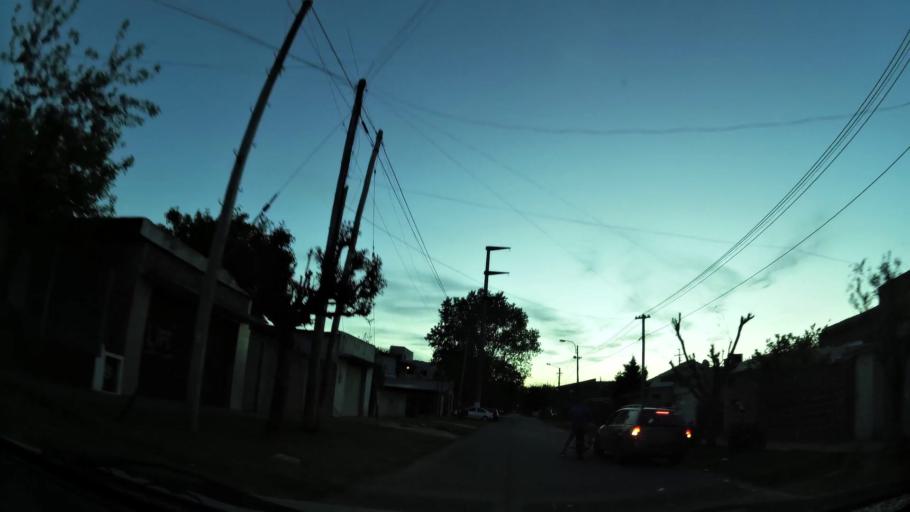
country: AR
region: Buenos Aires
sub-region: Partido de Quilmes
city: Quilmes
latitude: -34.7778
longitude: -58.2190
